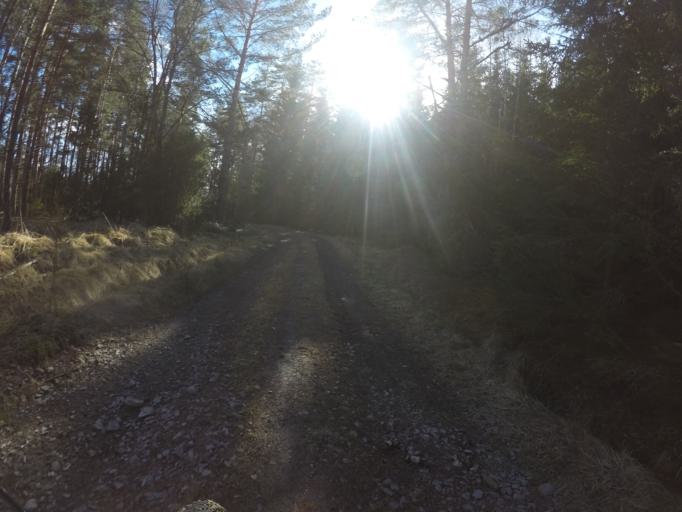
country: SE
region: Soedermanland
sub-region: Eskilstuna Kommun
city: Kvicksund
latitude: 59.4251
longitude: 16.2851
